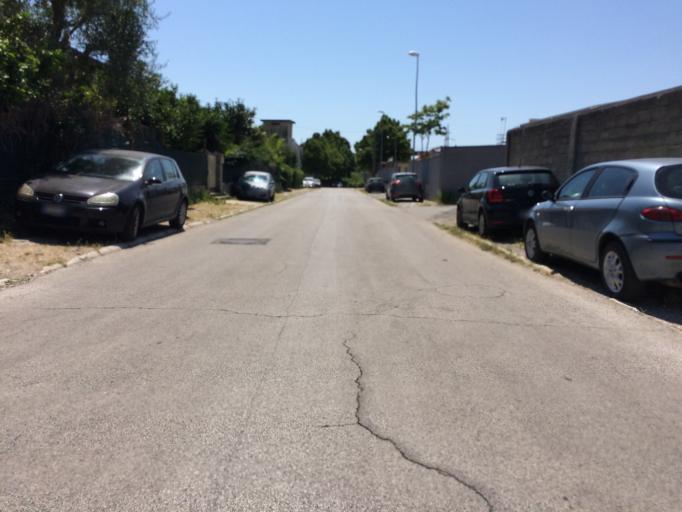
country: IT
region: Tuscany
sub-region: Provincia di Massa-Carrara
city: Massa
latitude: 44.0369
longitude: 10.1259
